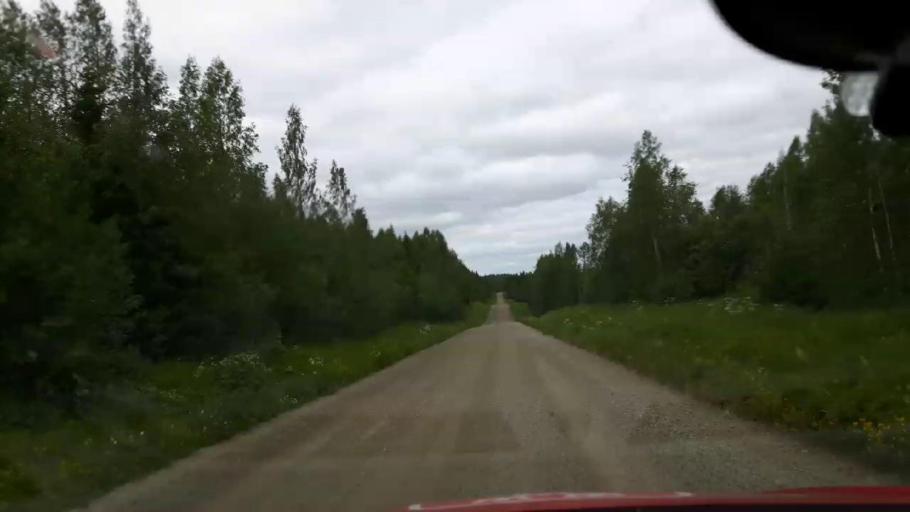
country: SE
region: Jaemtland
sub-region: OEstersunds Kommun
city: Brunflo
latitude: 62.9362
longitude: 14.9938
